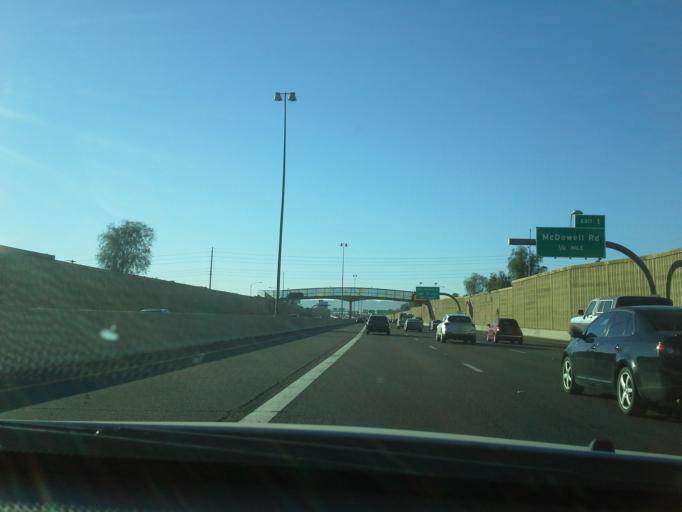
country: US
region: Arizona
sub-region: Maricopa County
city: Phoenix
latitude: 33.4746
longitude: -112.0386
